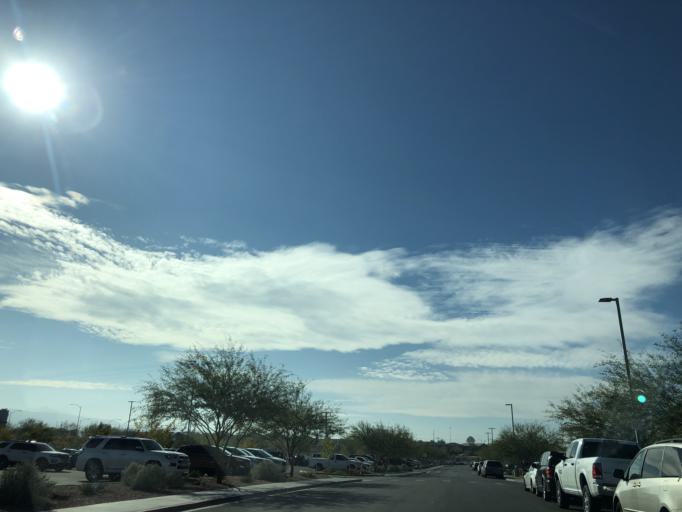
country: US
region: Nevada
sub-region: Clark County
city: Whitney
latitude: 36.0734
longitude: -115.0279
